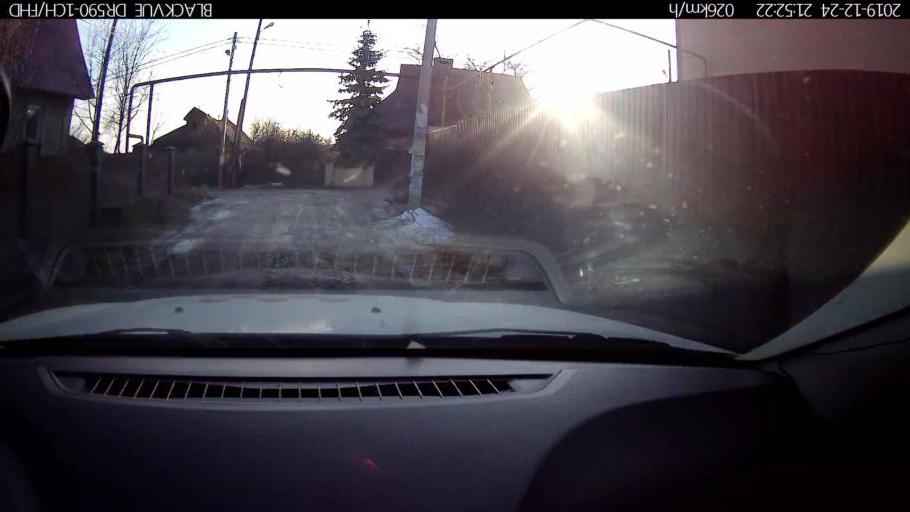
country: RU
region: Nizjnij Novgorod
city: Burevestnik
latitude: 56.2176
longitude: 43.8462
